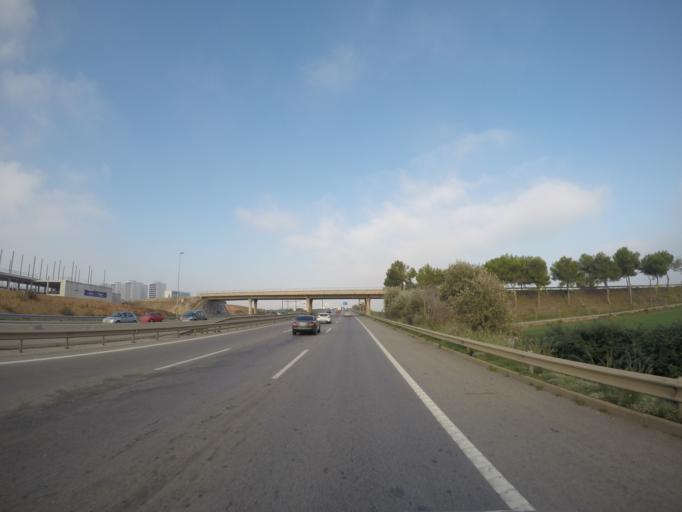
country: ES
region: Catalonia
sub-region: Provincia de Barcelona
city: Viladecans
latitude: 41.3065
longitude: 2.0277
